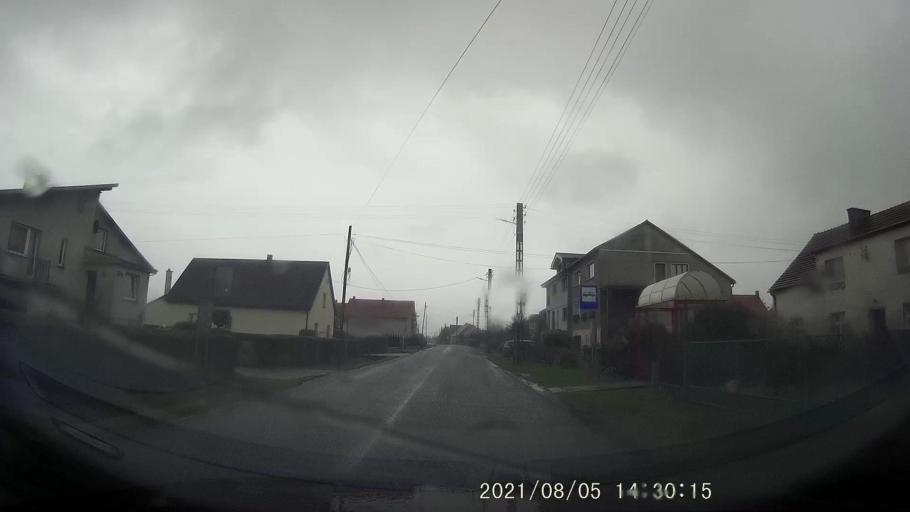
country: PL
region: Opole Voivodeship
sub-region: Powiat nyski
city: Korfantow
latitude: 50.4847
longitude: 17.5552
